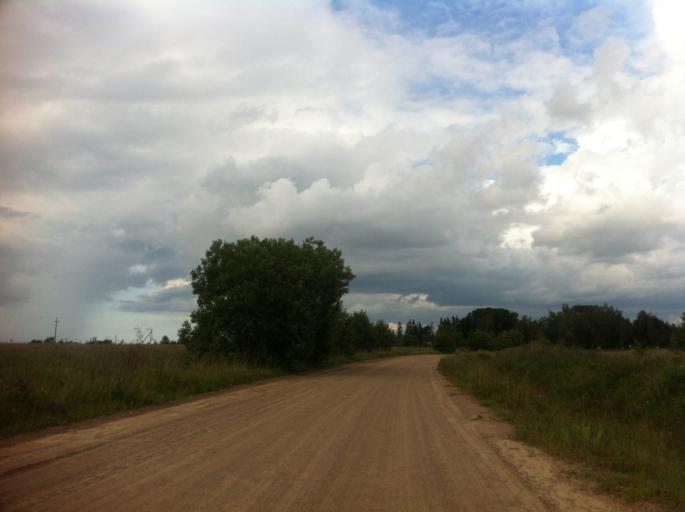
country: RU
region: Pskov
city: Izborsk
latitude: 57.8351
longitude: 27.9858
